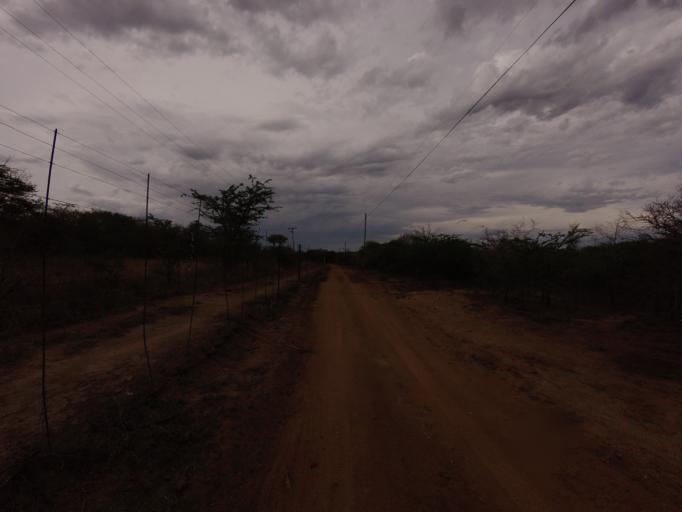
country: ZA
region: Limpopo
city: Thulamahashi
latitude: -24.5224
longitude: 31.1113
